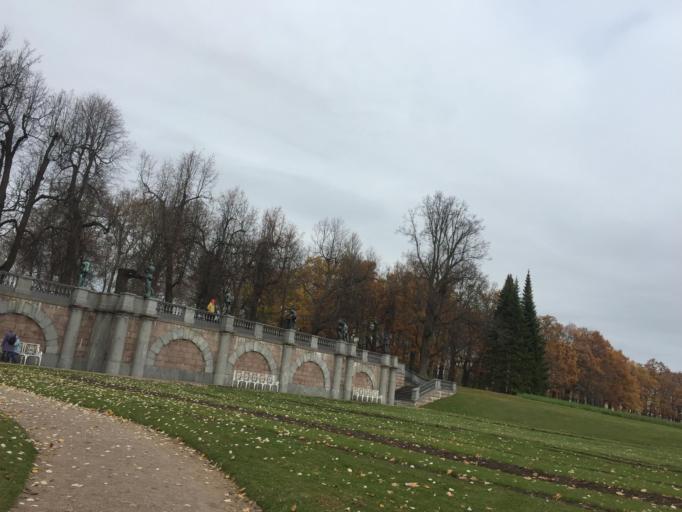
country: RU
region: St.-Petersburg
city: Pushkin
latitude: 59.7125
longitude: 30.3916
